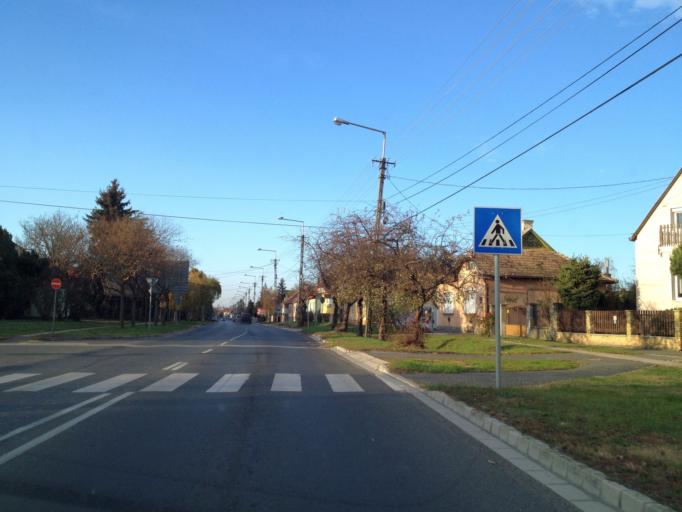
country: HU
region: Gyor-Moson-Sopron
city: Gyor
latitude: 47.6540
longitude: 17.6586
